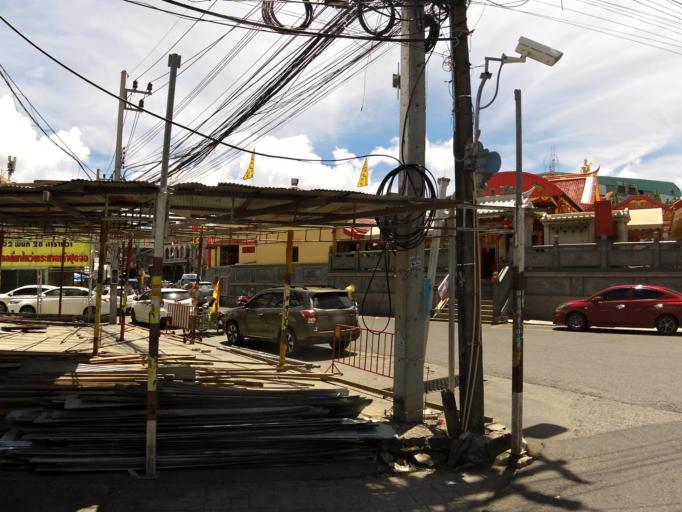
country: TH
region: Phuket
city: Ban Talat Nua
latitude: 7.8837
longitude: 98.3835
